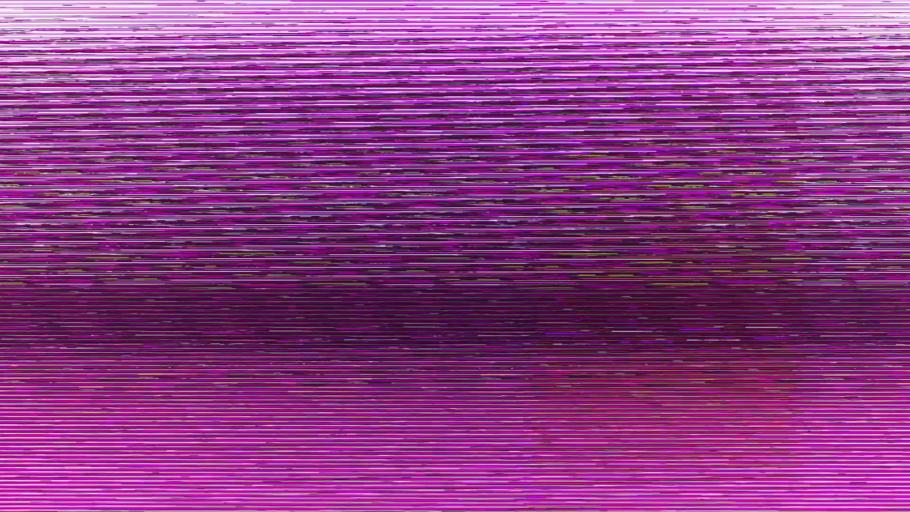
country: US
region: Michigan
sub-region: Washtenaw County
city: Ann Arbor
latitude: 42.3127
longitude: -83.6928
